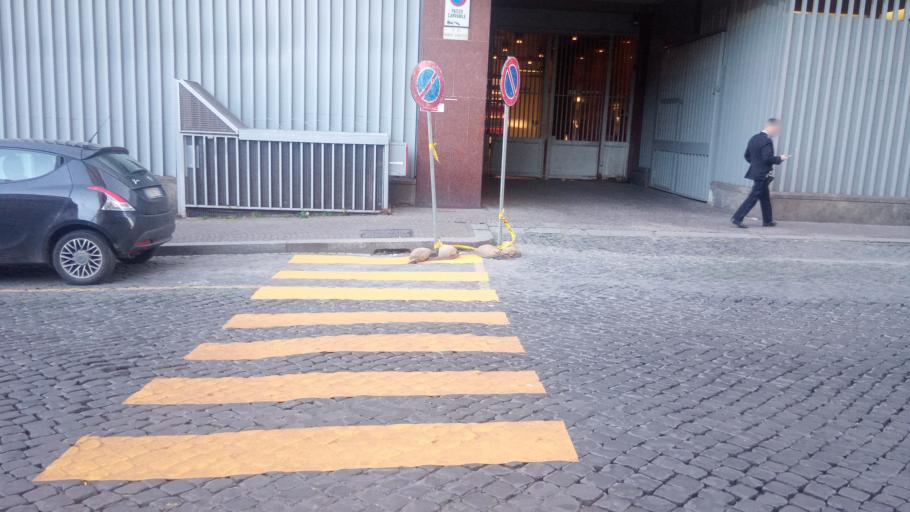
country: IT
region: Latium
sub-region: Citta metropolitana di Roma Capitale
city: Rome
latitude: 41.9003
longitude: 12.5057
